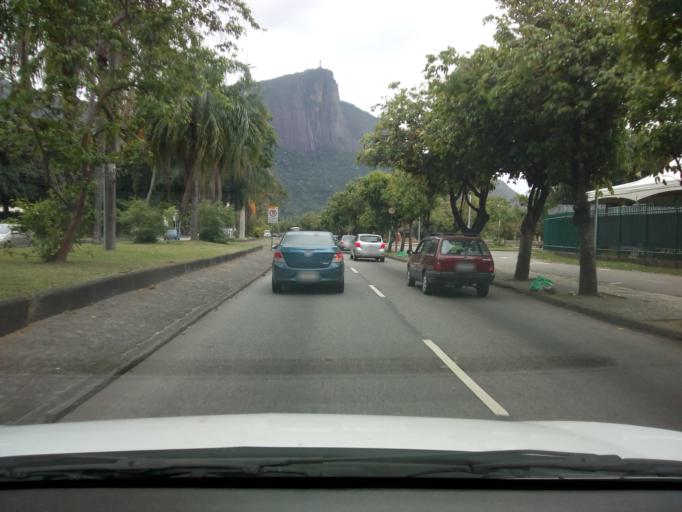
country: BR
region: Rio de Janeiro
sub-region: Rio De Janeiro
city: Rio de Janeiro
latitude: -22.9743
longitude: -43.2181
